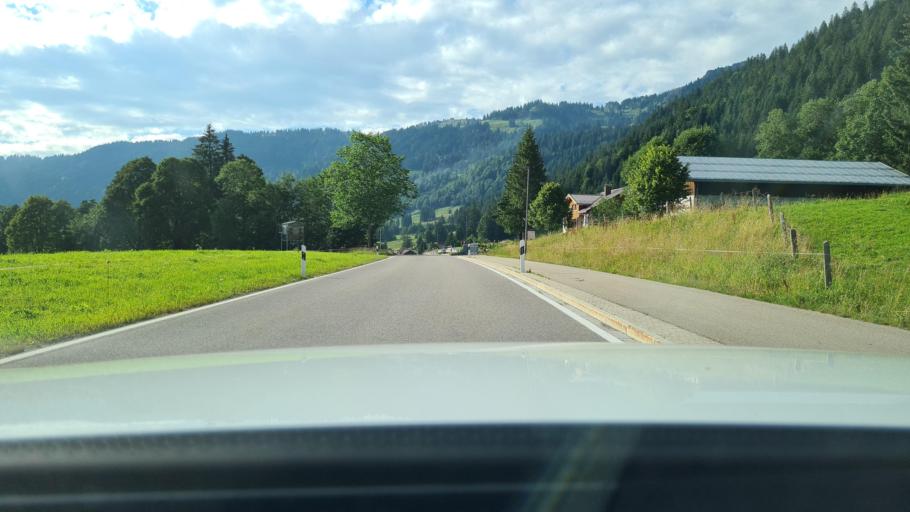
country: DE
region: Bavaria
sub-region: Swabia
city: Balderschwang
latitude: 47.4584
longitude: 10.1289
